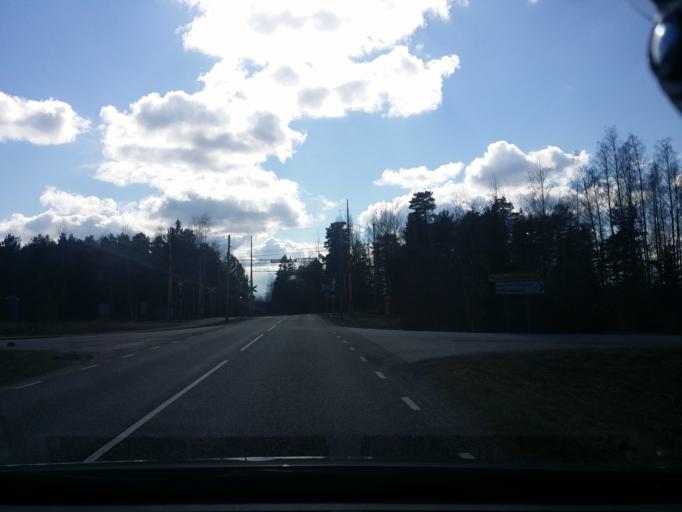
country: SE
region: Vaestmanland
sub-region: Sala Kommun
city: Sala
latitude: 59.9908
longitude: 16.4797
